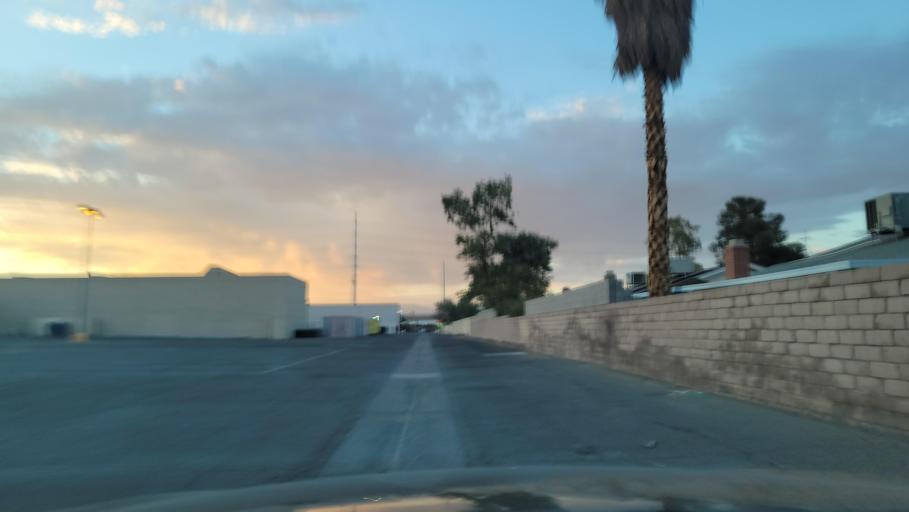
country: US
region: Nevada
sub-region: Clark County
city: Spring Valley
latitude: 36.1123
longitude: -115.2411
